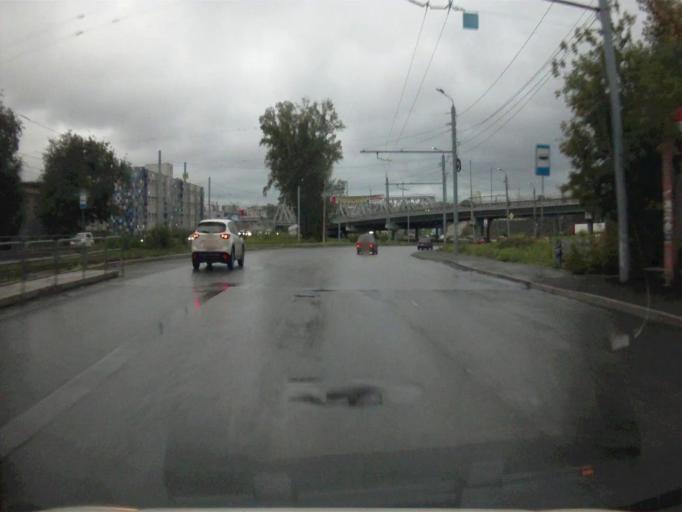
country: RU
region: Chelyabinsk
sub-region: Gorod Chelyabinsk
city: Chelyabinsk
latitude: 55.1576
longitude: 61.4444
